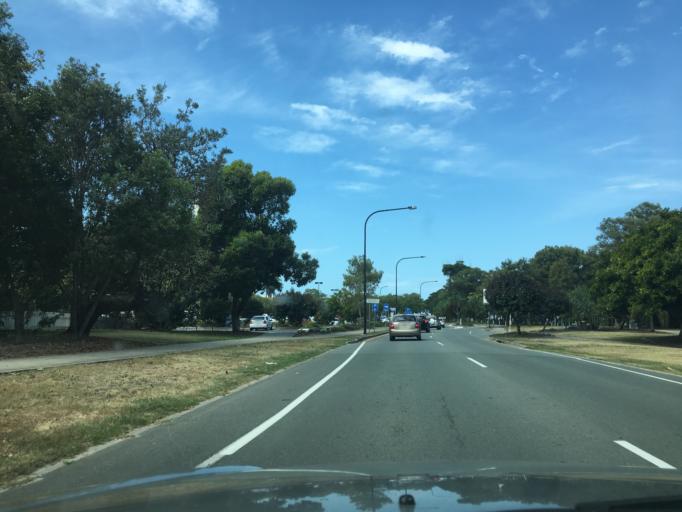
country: AU
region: Queensland
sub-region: Moreton Bay
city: Woorim
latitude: -27.0703
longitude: 153.2020
